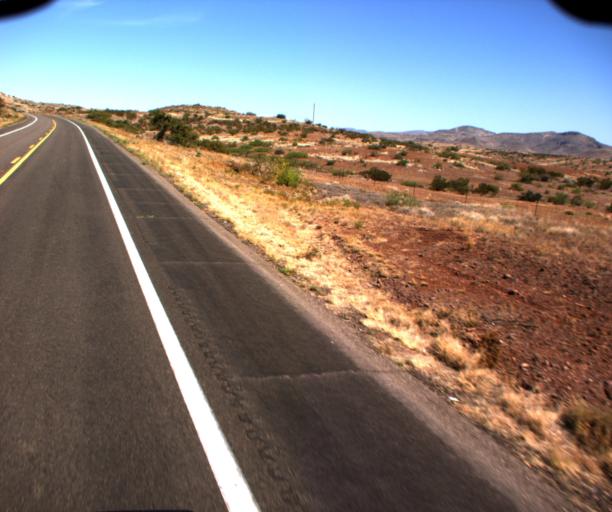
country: US
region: Arizona
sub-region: Greenlee County
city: Clifton
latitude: 32.7483
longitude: -109.2286
